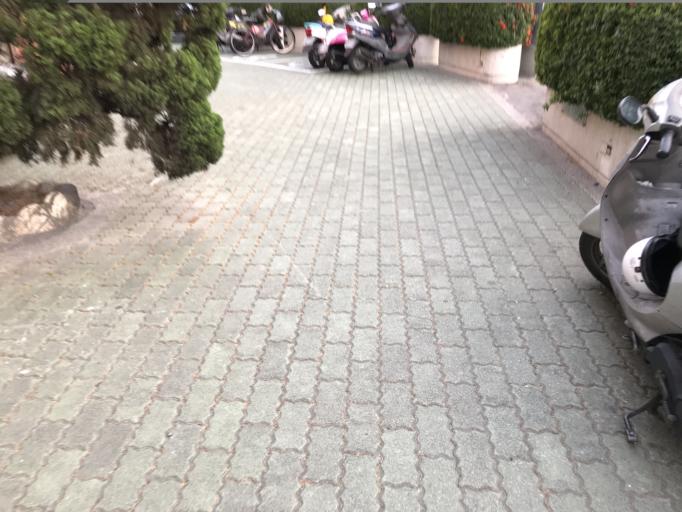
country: TW
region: Taiwan
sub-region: Tainan
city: Tainan
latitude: 22.9923
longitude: 120.2055
